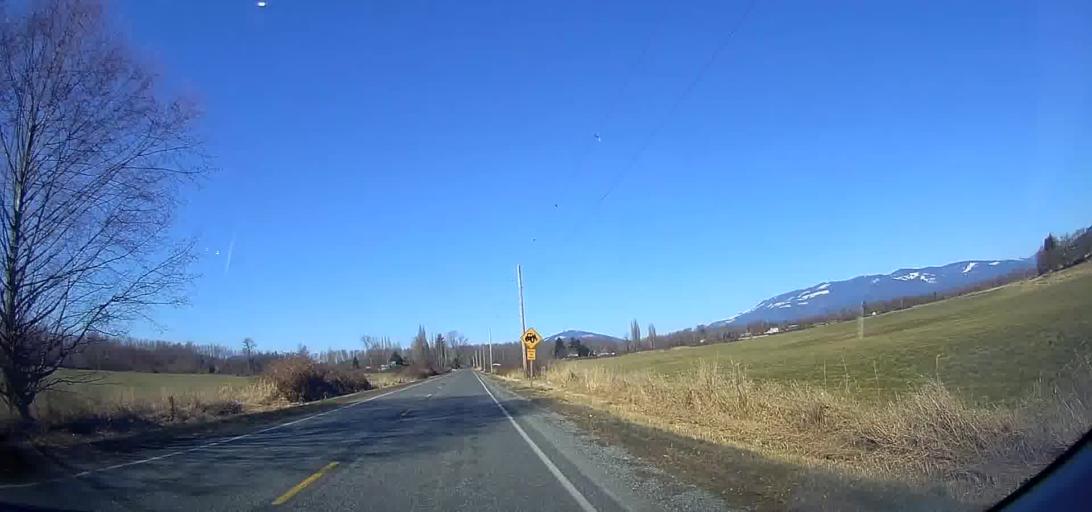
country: US
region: Washington
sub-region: Skagit County
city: Burlington
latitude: 48.4584
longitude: -122.3028
